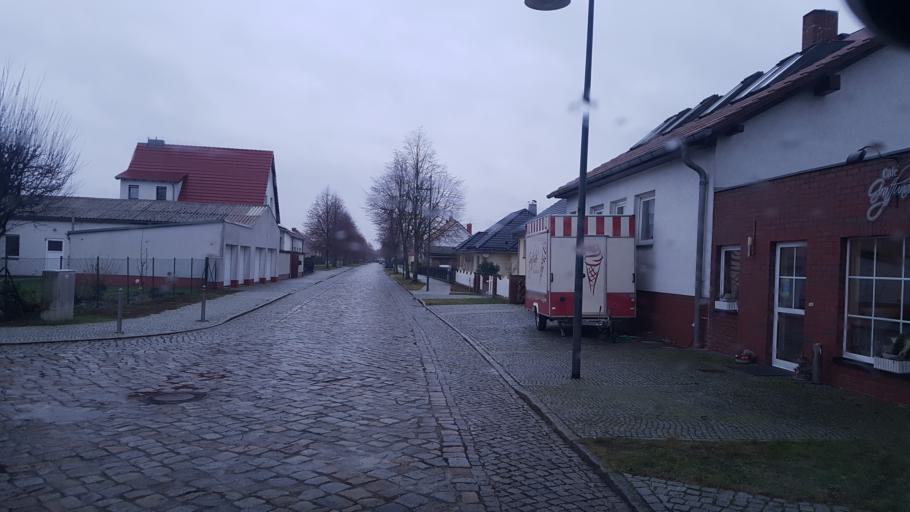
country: DE
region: Brandenburg
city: Ludwigsfelde
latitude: 52.3163
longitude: 13.1935
